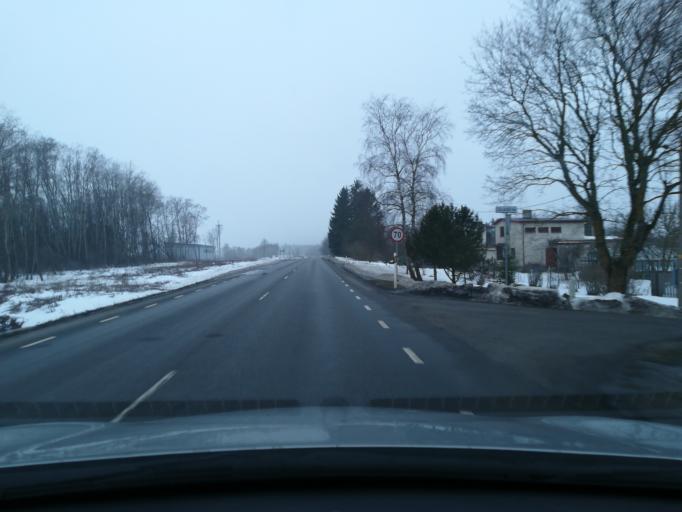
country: EE
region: Harju
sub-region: Raasiku vald
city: Raasiku
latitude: 59.3629
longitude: 25.1770
